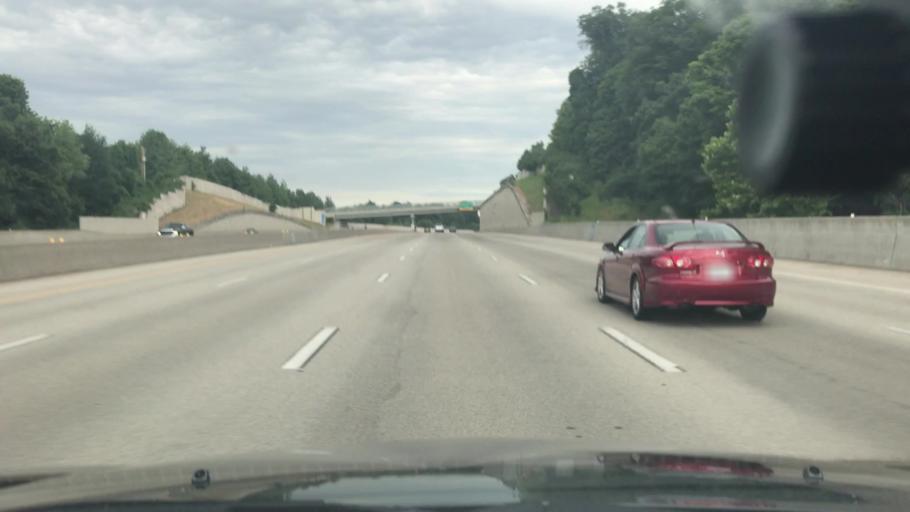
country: US
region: Missouri
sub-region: Saint Louis County
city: Maryland Heights
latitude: 38.7061
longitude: -90.4822
